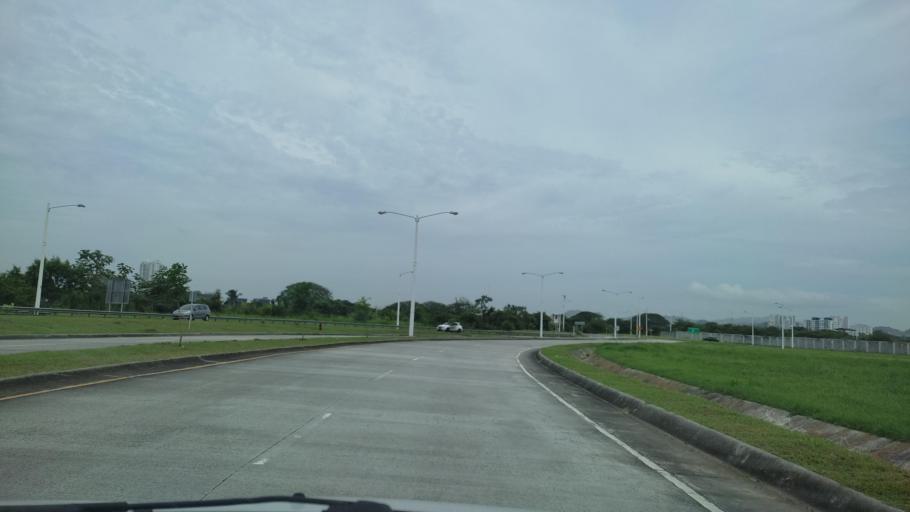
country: PA
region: Panama
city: San Miguelito
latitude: 9.0337
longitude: -79.4448
